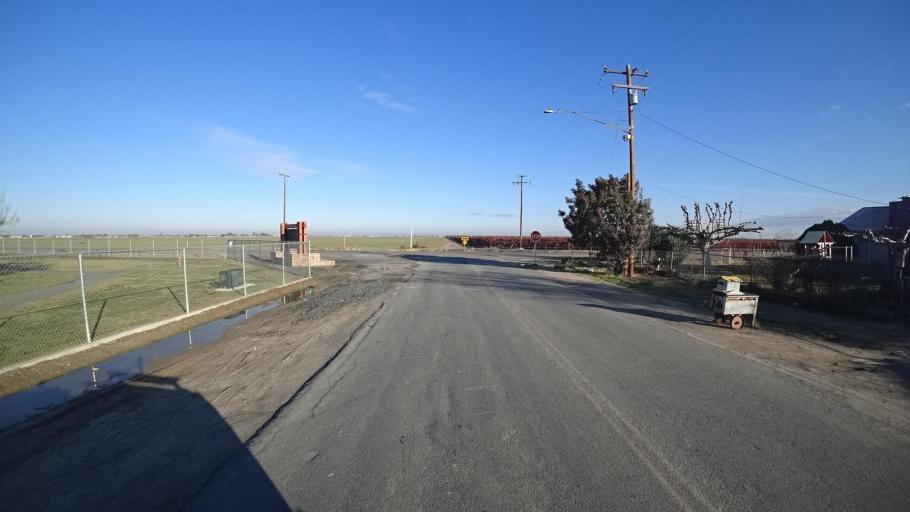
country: US
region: California
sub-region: Kern County
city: Delano
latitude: 35.7755
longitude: -119.2853
